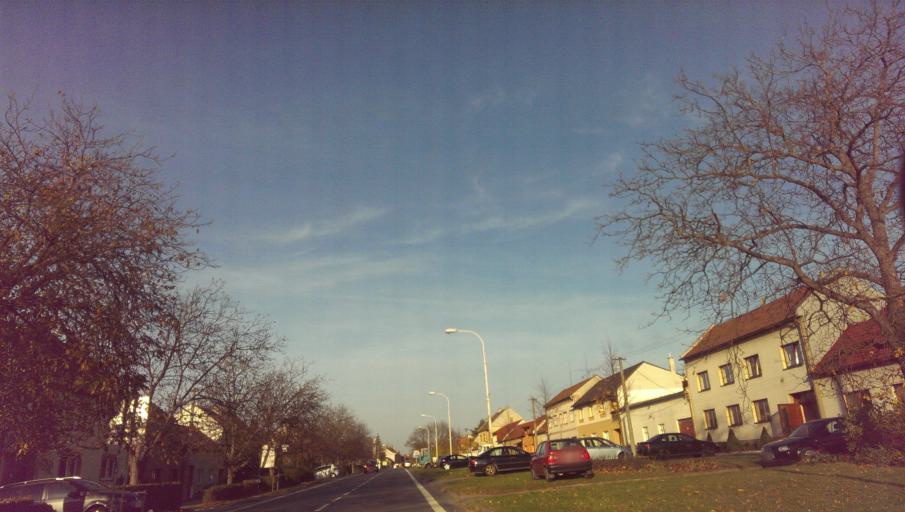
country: CZ
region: Zlin
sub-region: Okres Zlin
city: Ostrozska Nova Ves
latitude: 49.0031
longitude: 17.4330
